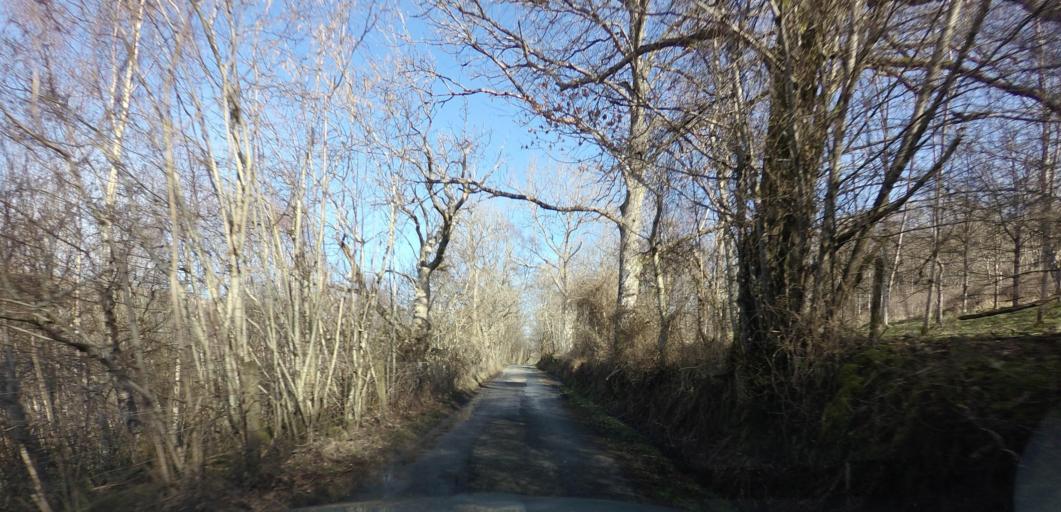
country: GB
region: Scotland
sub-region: Perth and Kinross
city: Comrie
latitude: 56.5431
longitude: -4.1003
